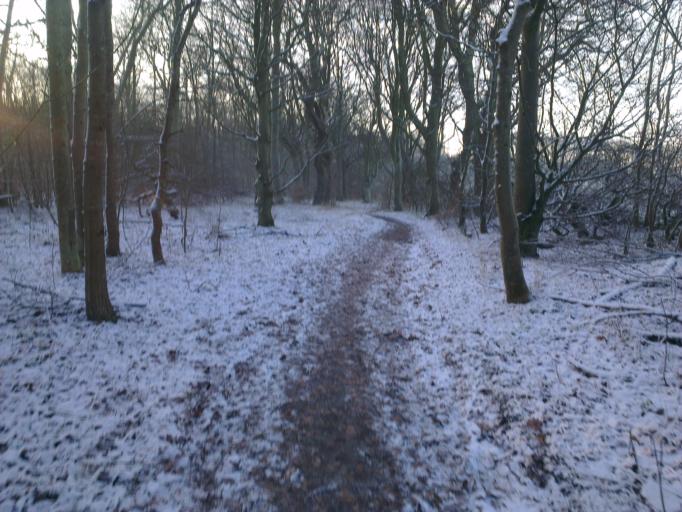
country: DK
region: Capital Region
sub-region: Frederikssund Kommune
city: Jaegerspris
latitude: 55.8633
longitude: 11.9752
